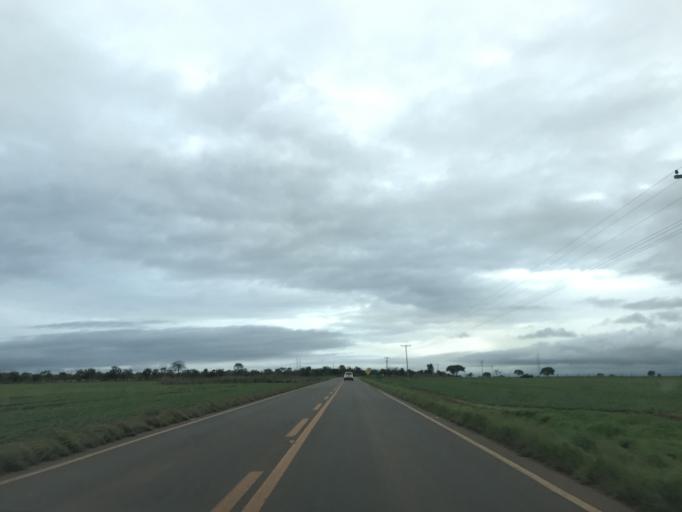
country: BR
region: Goias
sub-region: Luziania
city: Luziania
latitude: -16.2966
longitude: -48.0086
